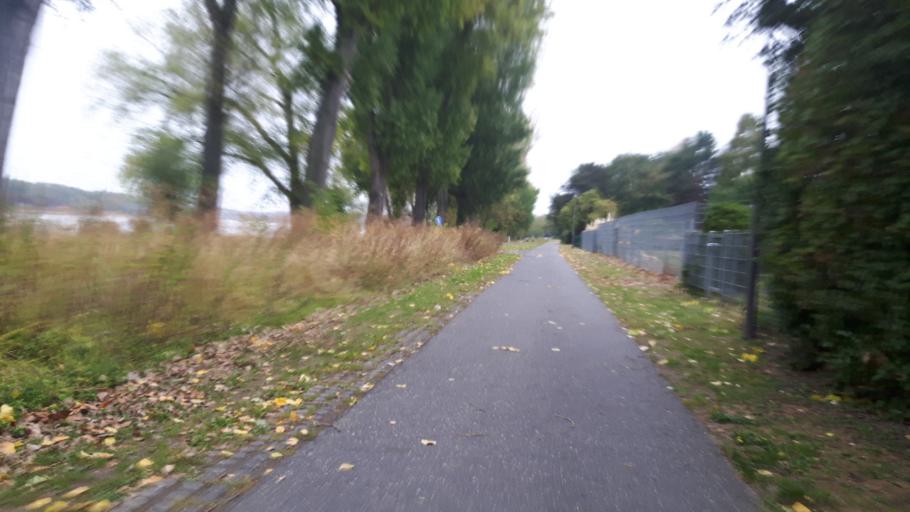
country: DE
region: North Rhine-Westphalia
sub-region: Regierungsbezirk Koln
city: Konigswinter
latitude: 50.6969
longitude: 7.1747
